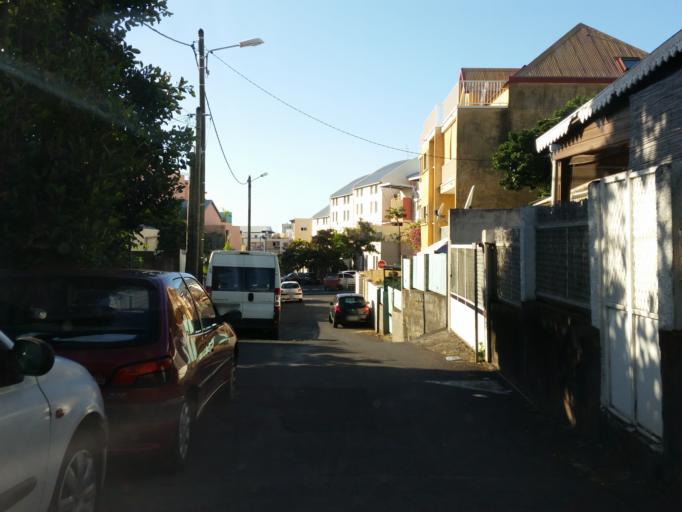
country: RE
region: Reunion
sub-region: Reunion
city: Saint-Denis
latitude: -20.8975
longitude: 55.4696
